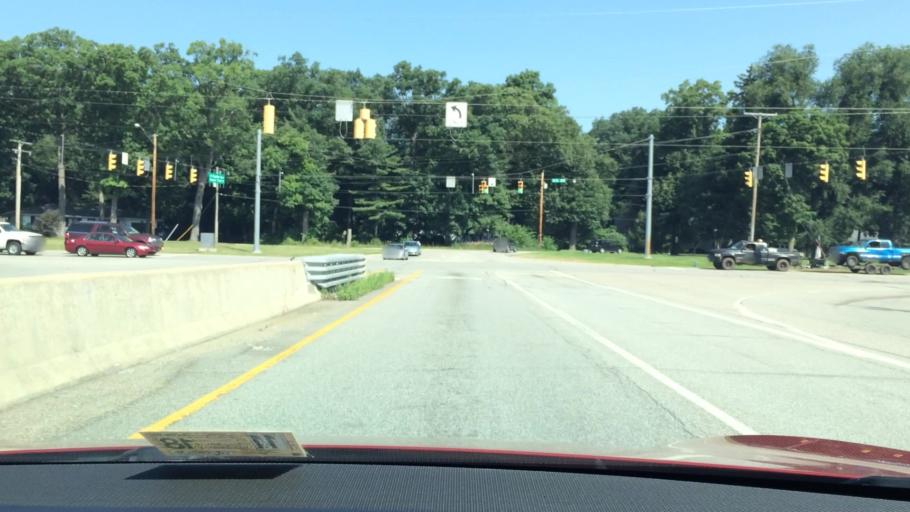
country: US
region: Indiana
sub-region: Saint Joseph County
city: Granger
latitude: 41.7362
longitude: -86.1517
